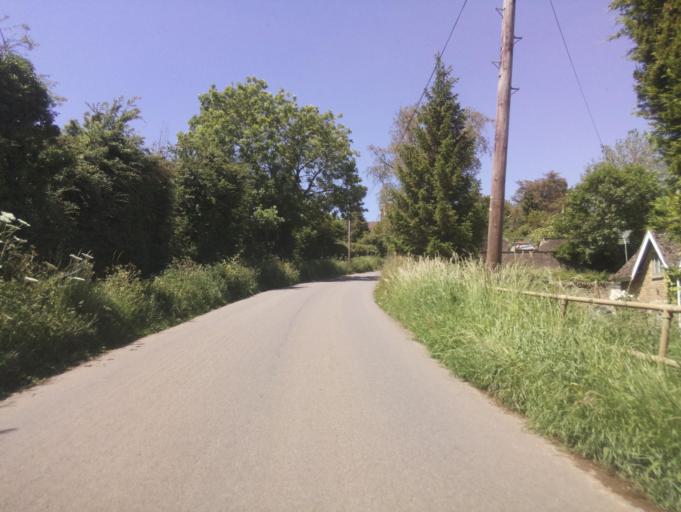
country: GB
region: England
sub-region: Wiltshire
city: Bremhill
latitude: 51.4528
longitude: -2.0353
